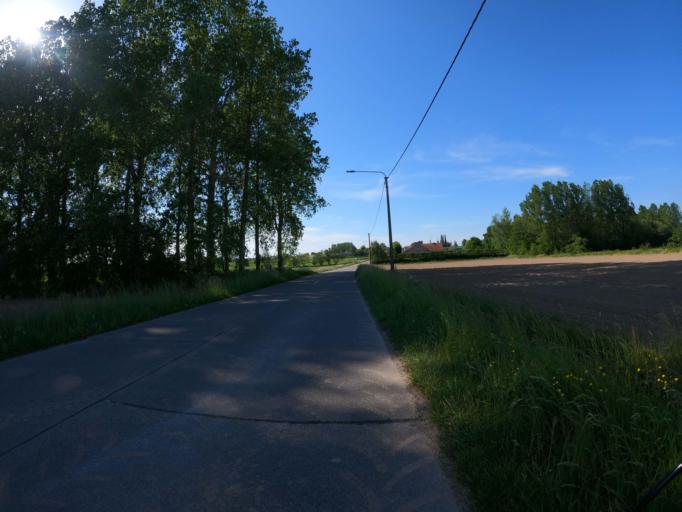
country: BE
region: Flanders
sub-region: Provincie Oost-Vlaanderen
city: Oosterzele
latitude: 50.9382
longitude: 3.7492
